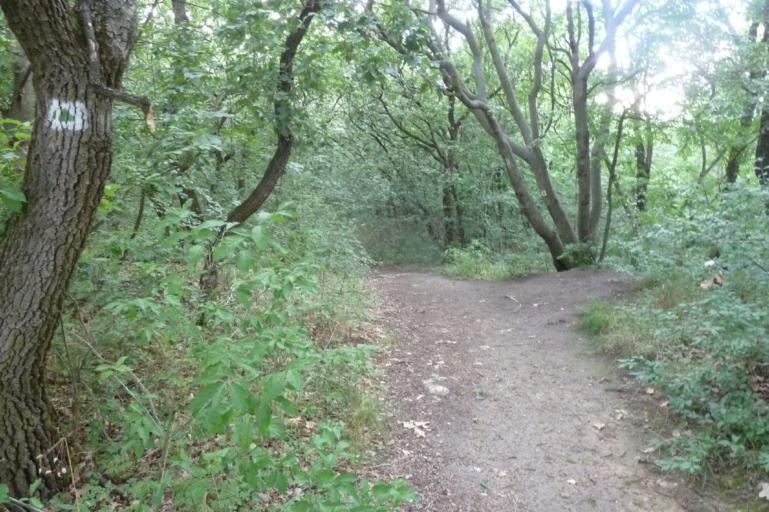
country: HU
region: Pest
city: Fot
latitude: 47.6269
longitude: 19.2149
